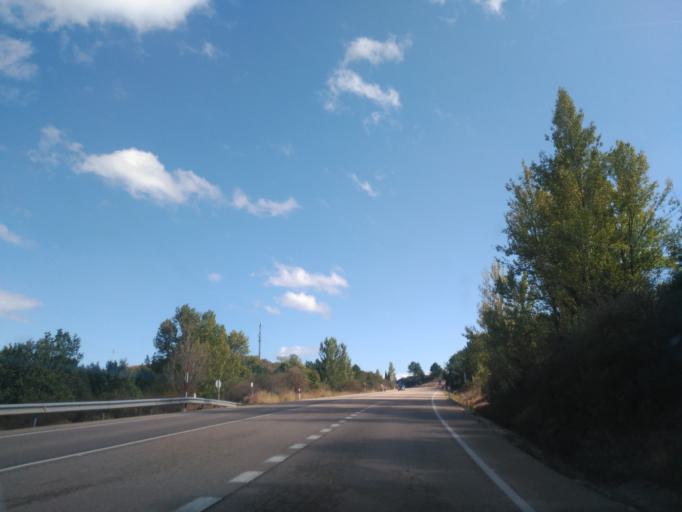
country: ES
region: Castille and Leon
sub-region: Provincia de Burgos
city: Pinilla de los Barruecos
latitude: 41.9020
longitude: -3.2721
